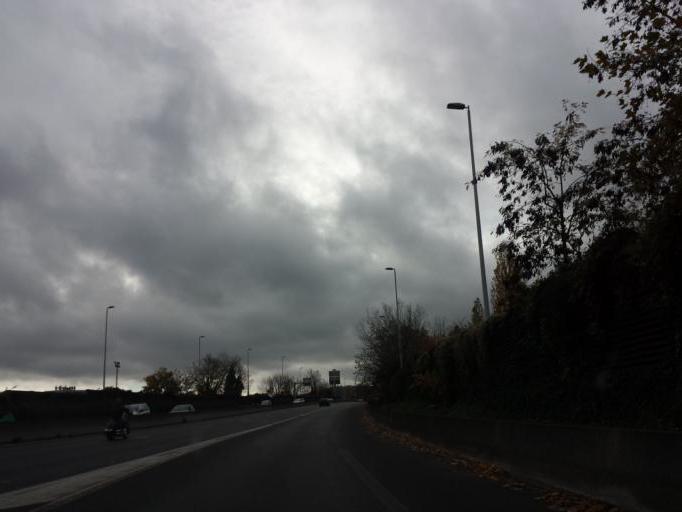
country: FR
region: Ile-de-France
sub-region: Departement du Val-d'Oise
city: Ermont
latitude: 48.9965
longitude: 2.2464
